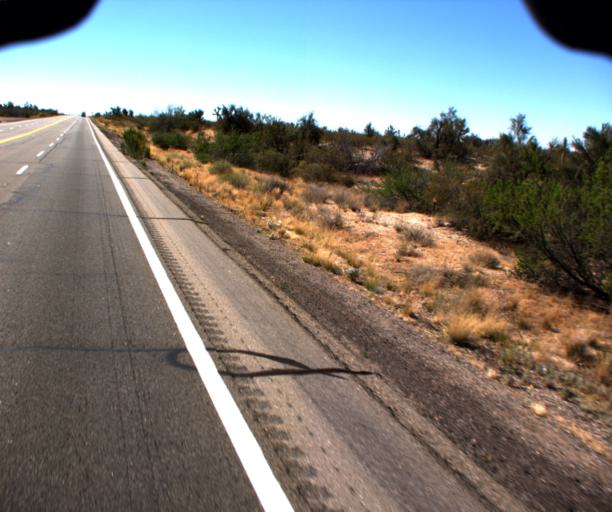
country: US
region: Arizona
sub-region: Yavapai County
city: Congress
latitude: 34.2820
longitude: -113.1036
